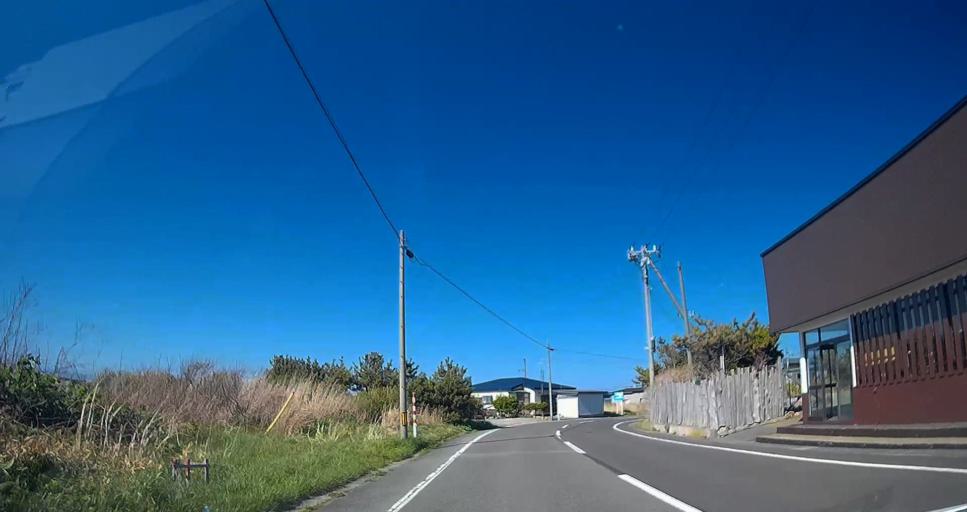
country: JP
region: Hokkaido
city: Hakodate
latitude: 41.5435
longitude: 140.9131
